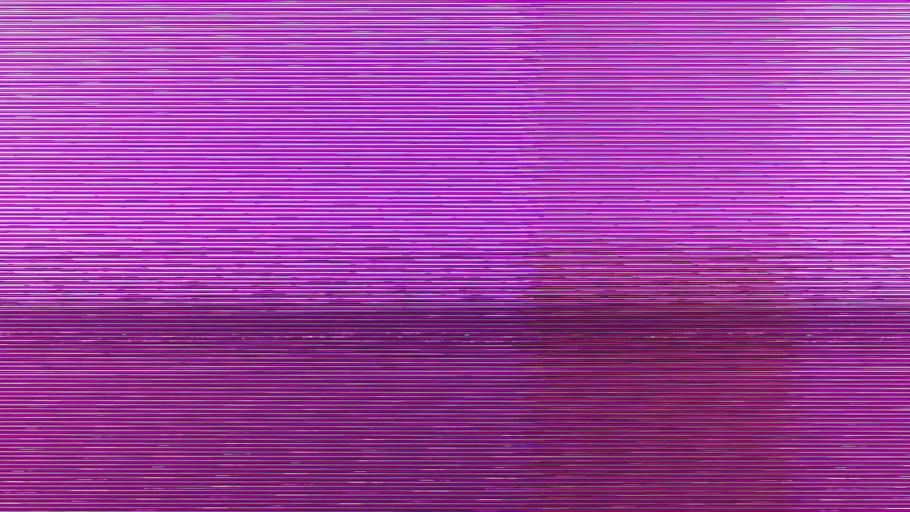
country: US
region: Wisconsin
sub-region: Racine County
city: Waterford
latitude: 42.7535
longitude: -88.2078
